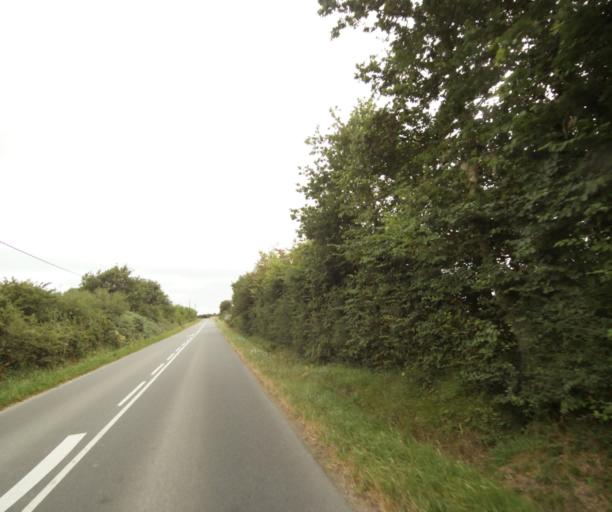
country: FR
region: Pays de la Loire
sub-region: Departement de la Vendee
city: Sainte-Foy
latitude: 46.5072
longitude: -1.6882
